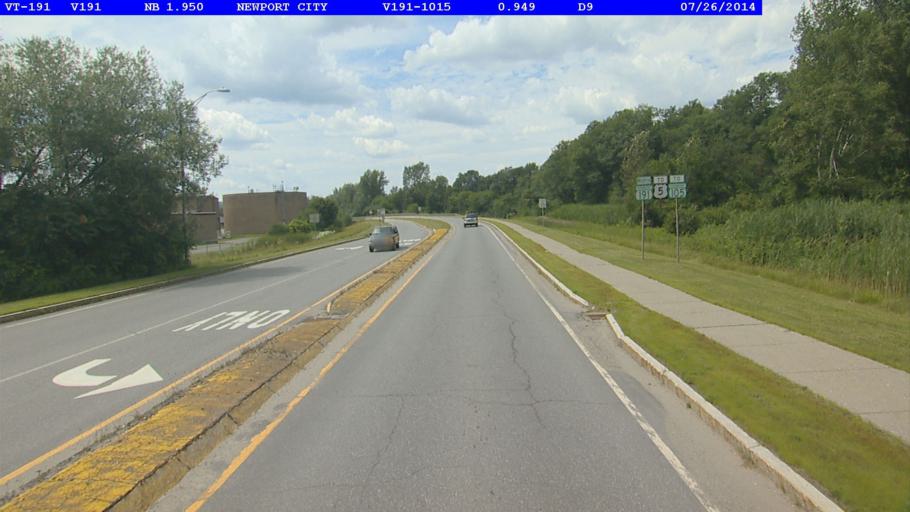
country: US
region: Vermont
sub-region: Orleans County
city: Newport
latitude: 44.9399
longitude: -72.1979
